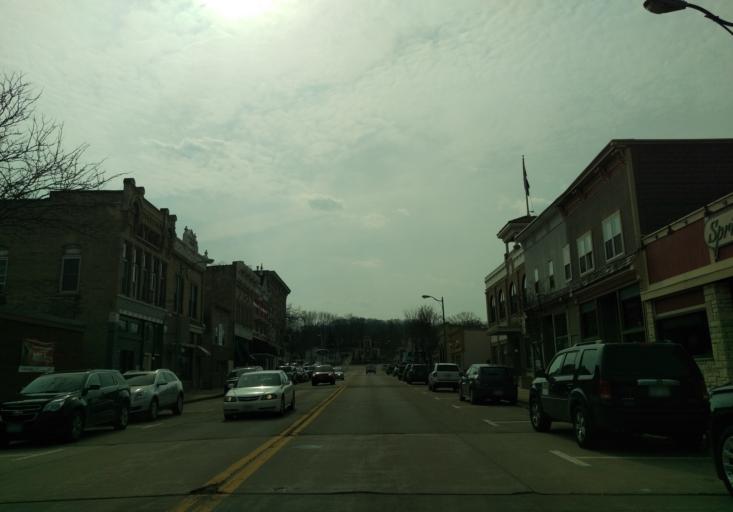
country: US
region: Wisconsin
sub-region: Columbia County
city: Lodi
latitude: 43.3135
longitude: -89.5264
